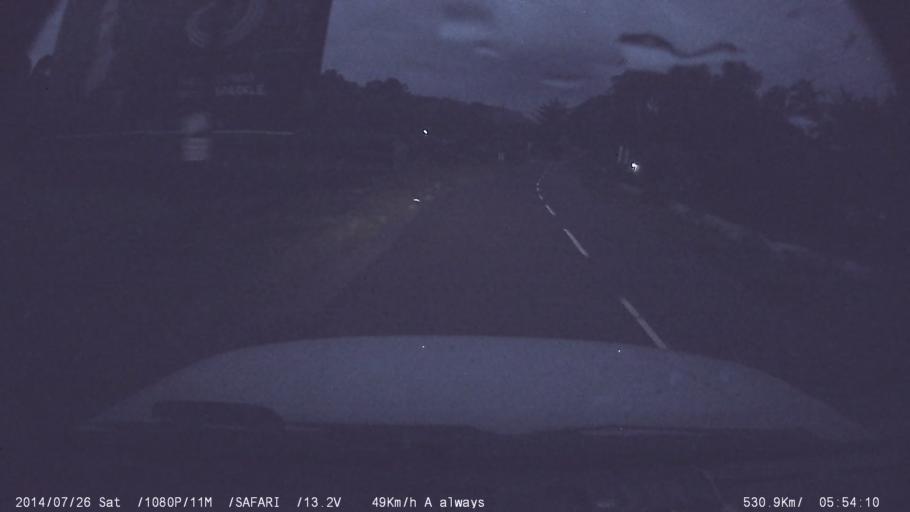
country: IN
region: Kerala
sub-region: Ernakulam
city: Muvattupuzha
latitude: 9.9494
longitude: 76.5762
